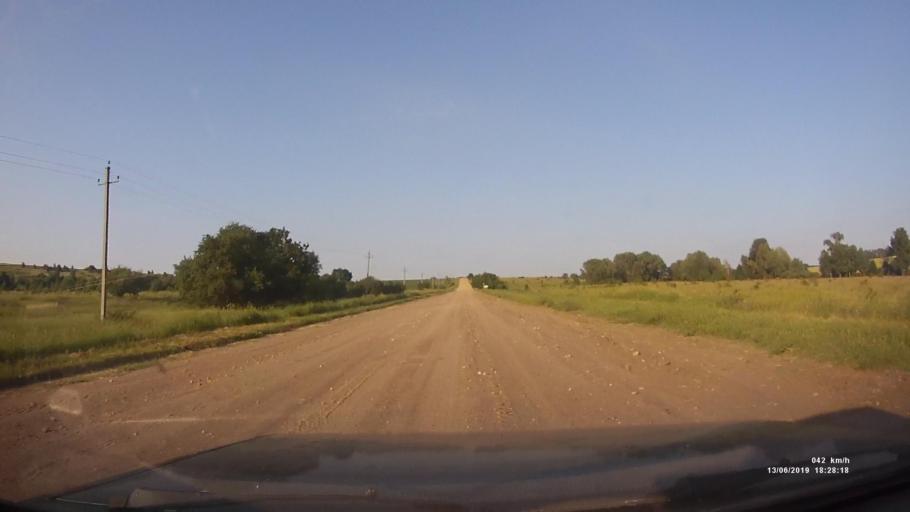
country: RU
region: Rostov
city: Kazanskaya
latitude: 49.8564
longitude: 41.3310
